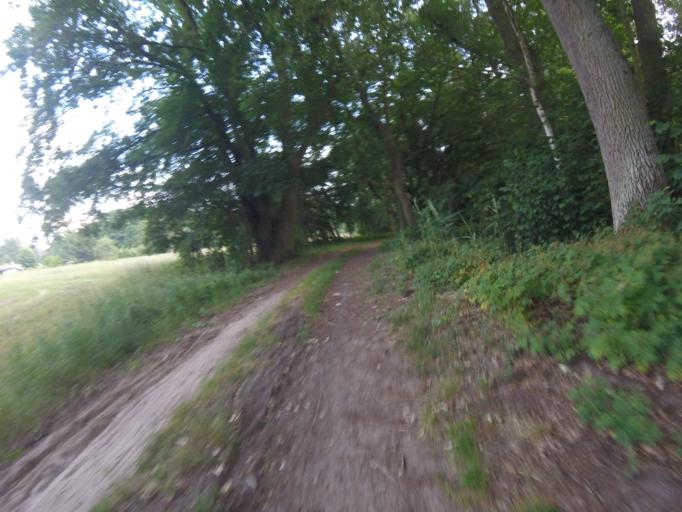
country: DE
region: Brandenburg
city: Bestensee
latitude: 52.2697
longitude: 13.6368
